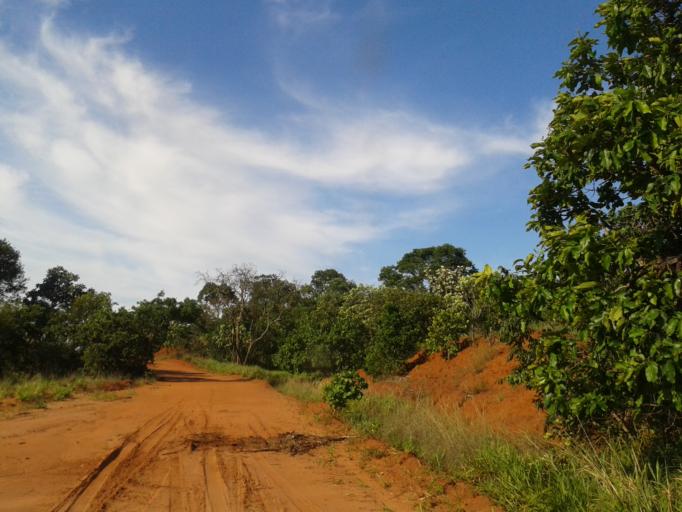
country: BR
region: Minas Gerais
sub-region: Santa Vitoria
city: Santa Vitoria
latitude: -19.1190
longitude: -49.9961
